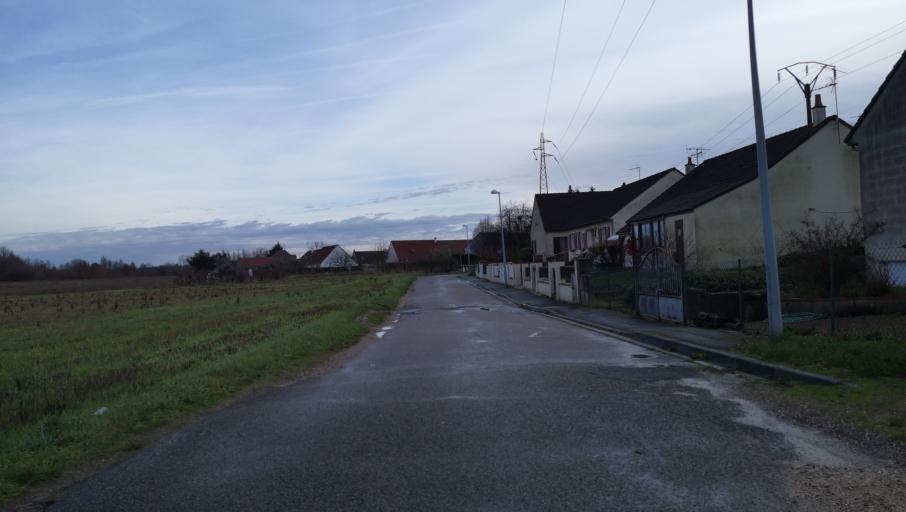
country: FR
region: Centre
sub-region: Departement du Loiret
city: Saint-Jean-de-Braye
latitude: 47.9230
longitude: 1.9634
